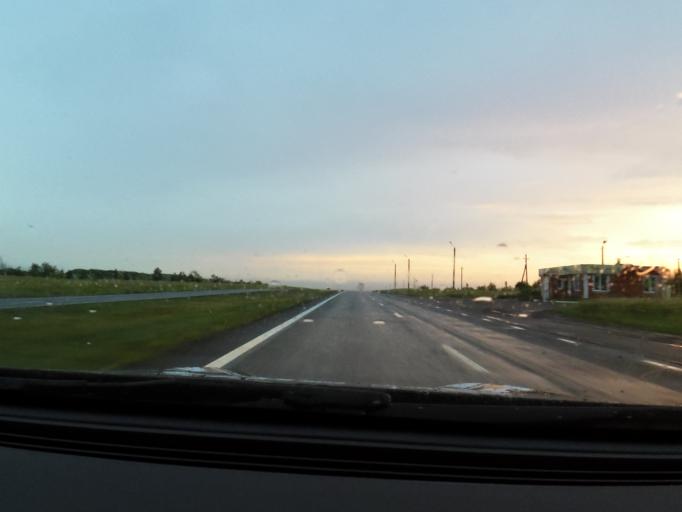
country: RU
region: Tatarstan
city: Yelabuga
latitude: 55.8141
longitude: 52.0412
